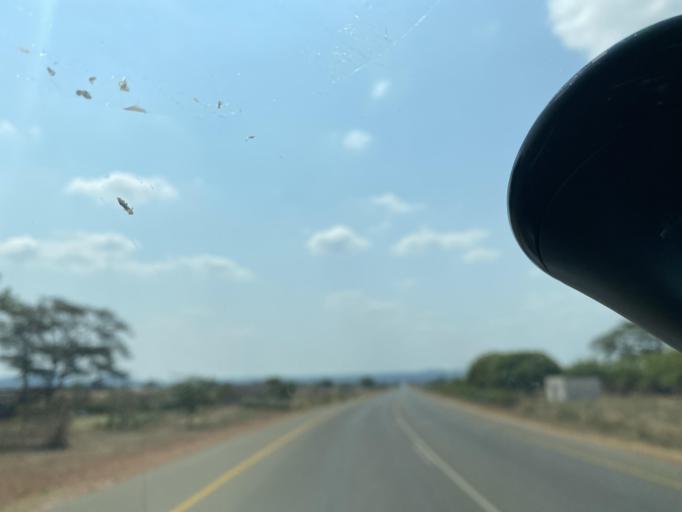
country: ZM
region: Lusaka
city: Chongwe
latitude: -15.5731
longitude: 28.6975
